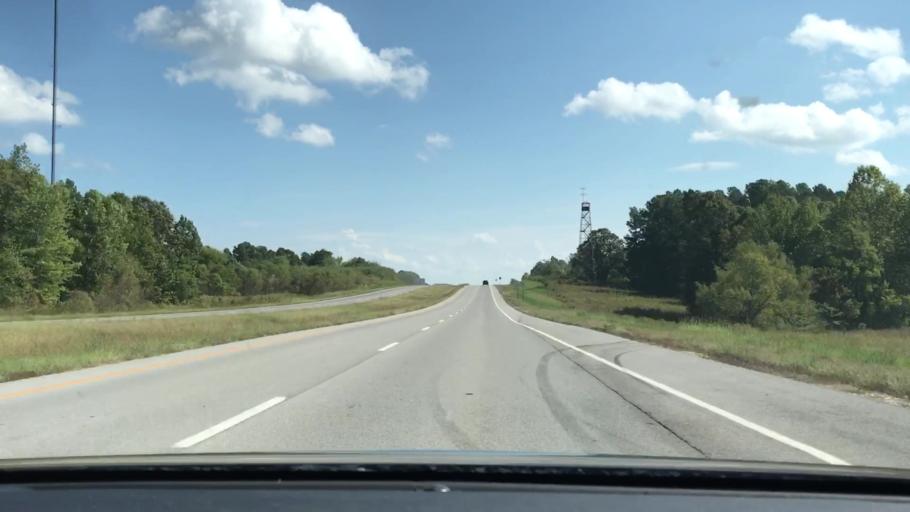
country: US
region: Kentucky
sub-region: Trigg County
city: Cadiz
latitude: 36.7801
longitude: -88.0607
